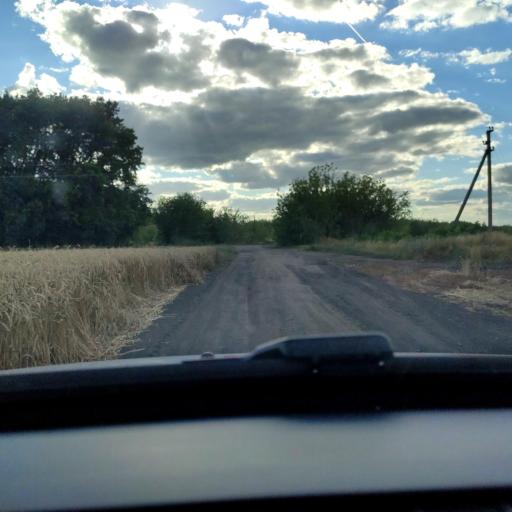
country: RU
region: Voronezj
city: Verkhnyaya Khava
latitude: 51.6109
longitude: 39.8216
